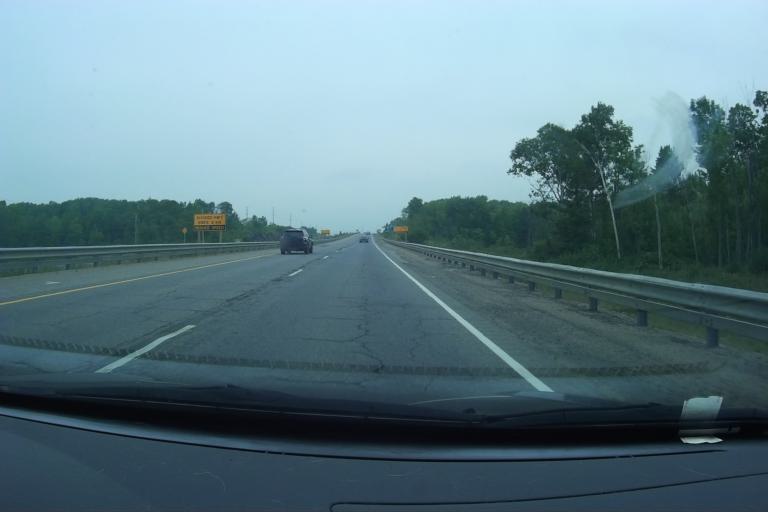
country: CA
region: Ontario
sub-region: Nipissing District
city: North Bay
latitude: 46.2916
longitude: -79.4206
